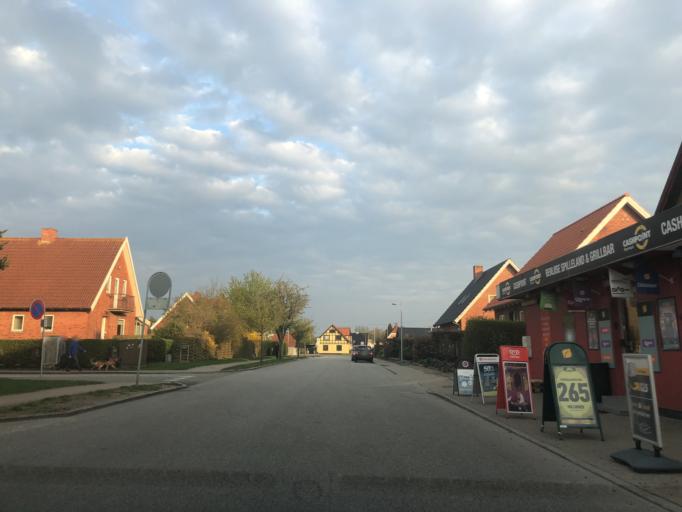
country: DK
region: Zealand
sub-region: Ringsted Kommune
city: Ringsted
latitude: 55.4595
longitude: 11.7934
